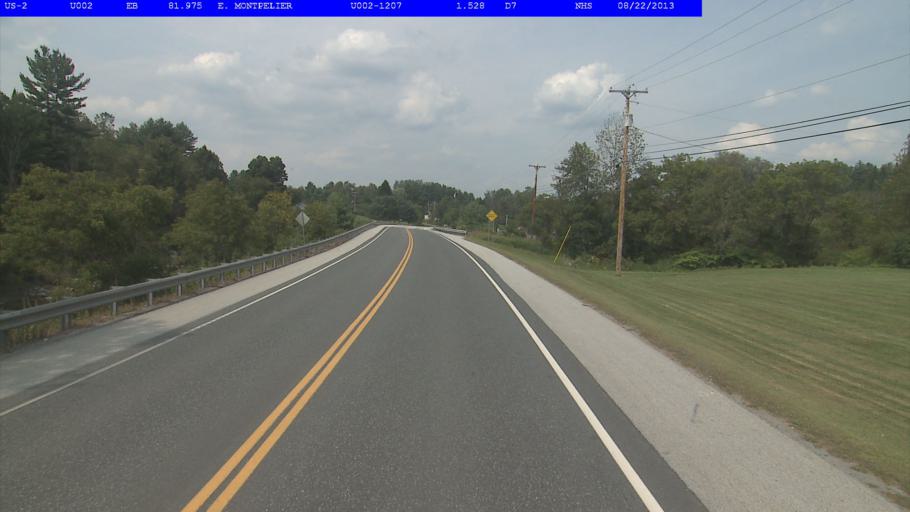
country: US
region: Vermont
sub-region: Washington County
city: Barre
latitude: 44.2551
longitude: -72.5019
